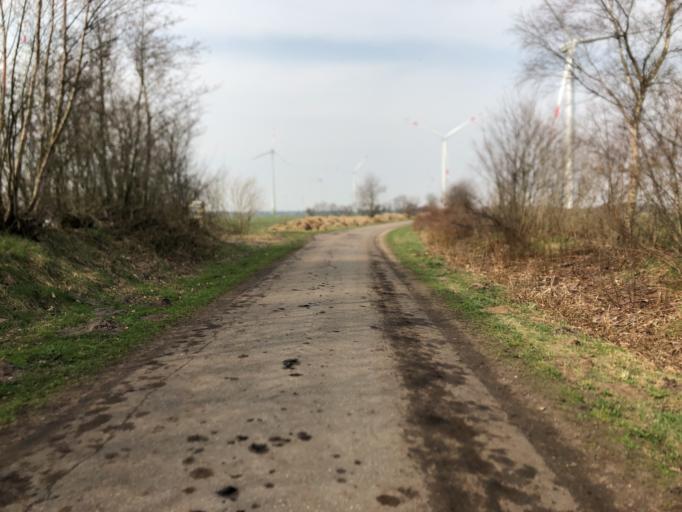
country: DE
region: Schleswig-Holstein
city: Wanderup
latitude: 54.6830
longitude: 9.3052
